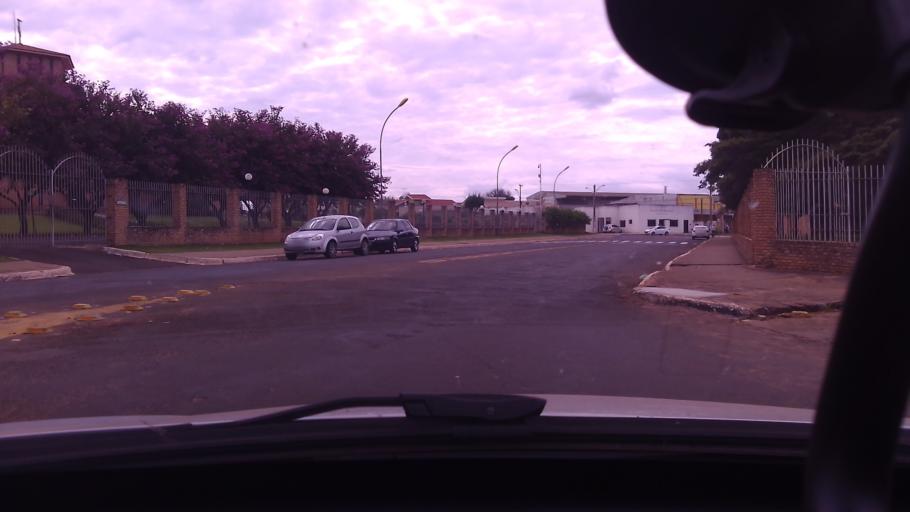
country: BR
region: Goias
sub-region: Mineiros
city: Mineiros
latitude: -17.5680
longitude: -52.5663
